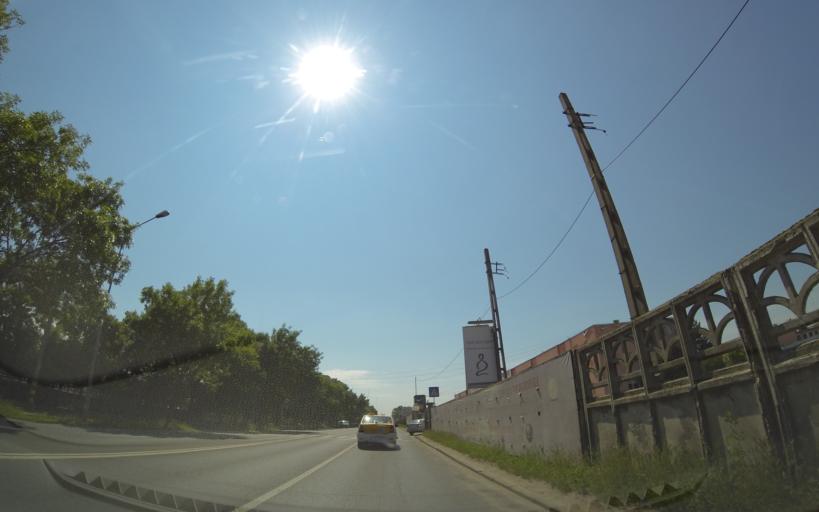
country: RO
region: Bucuresti
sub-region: Municipiul Bucuresti
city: Bucuresti
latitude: 44.4179
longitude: 26.0755
